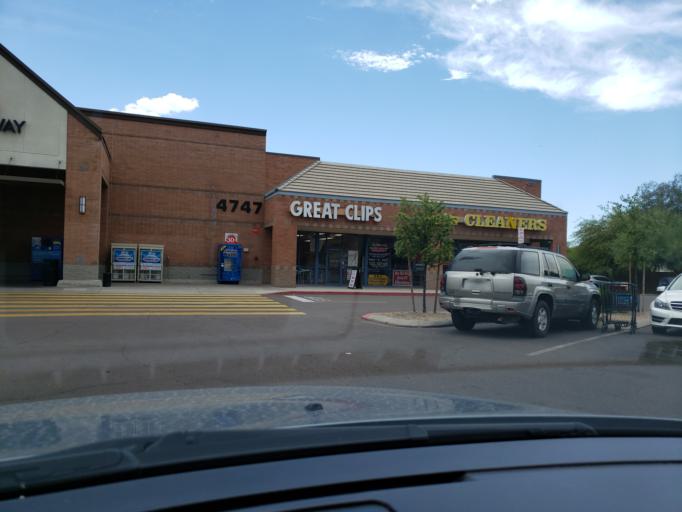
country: US
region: Arizona
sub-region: Maricopa County
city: Paradise Valley
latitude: 33.6250
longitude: -111.9793
